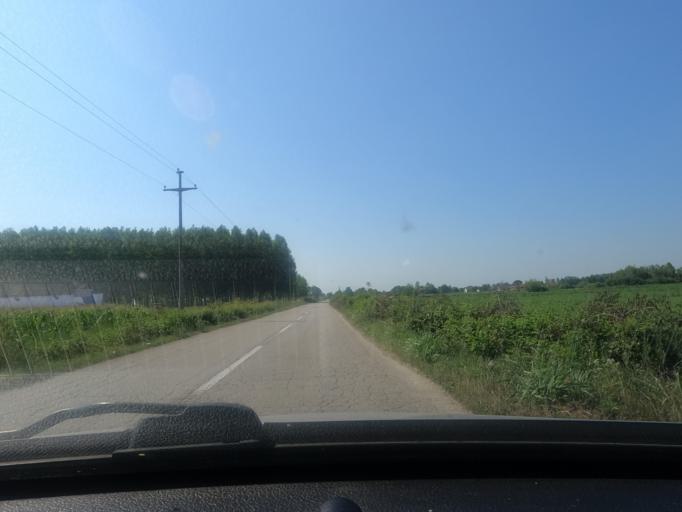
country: RS
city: Kozjak
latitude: 44.5736
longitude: 19.2791
